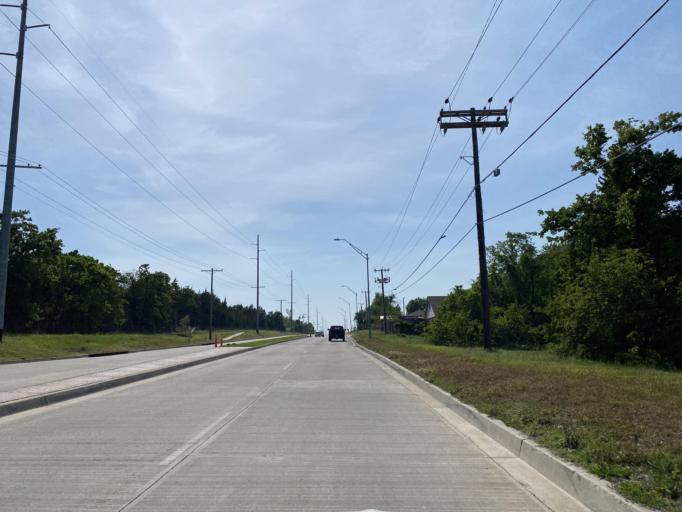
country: US
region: Oklahoma
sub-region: Oklahoma County
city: Nicoma Park
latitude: 35.4500
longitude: -97.3362
